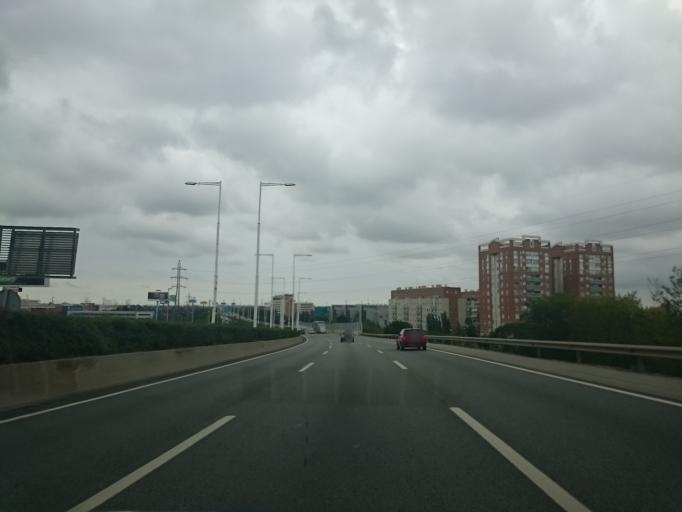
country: ES
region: Catalonia
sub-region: Provincia de Barcelona
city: Cornella de Llobregat
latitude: 41.3586
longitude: 2.0882
